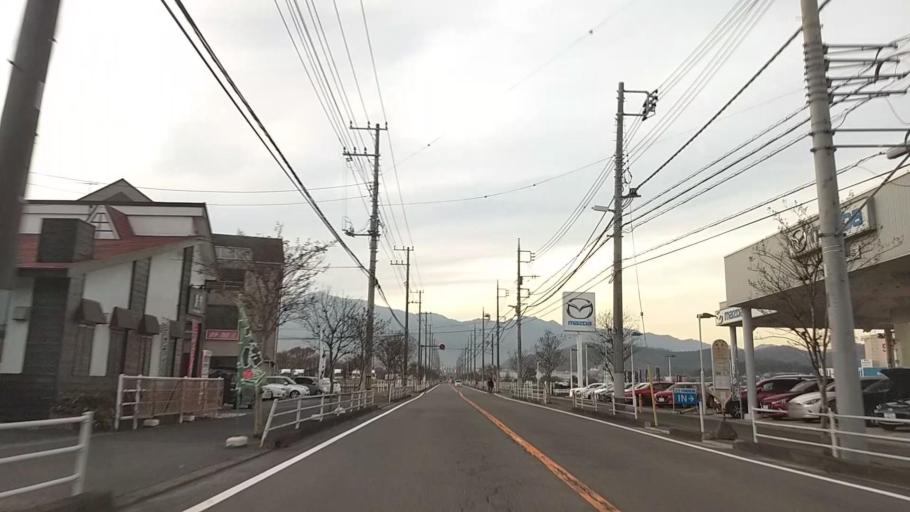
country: JP
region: Kanagawa
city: Atsugi
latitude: 35.4292
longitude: 139.3358
